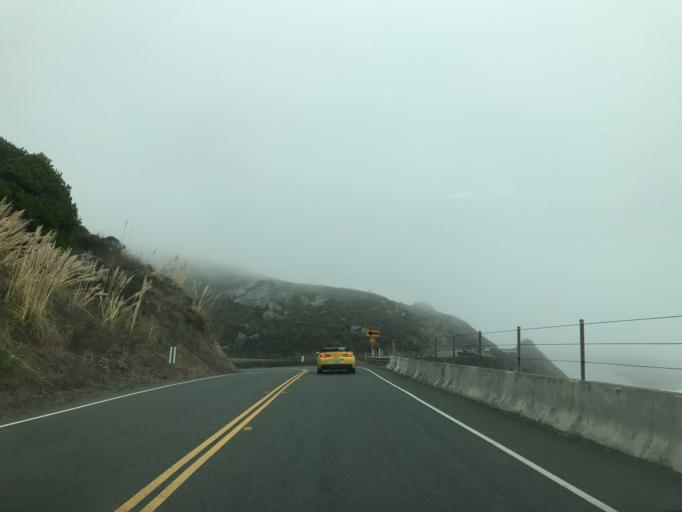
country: US
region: California
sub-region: Sonoma County
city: Monte Rio
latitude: 38.4553
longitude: -123.1346
